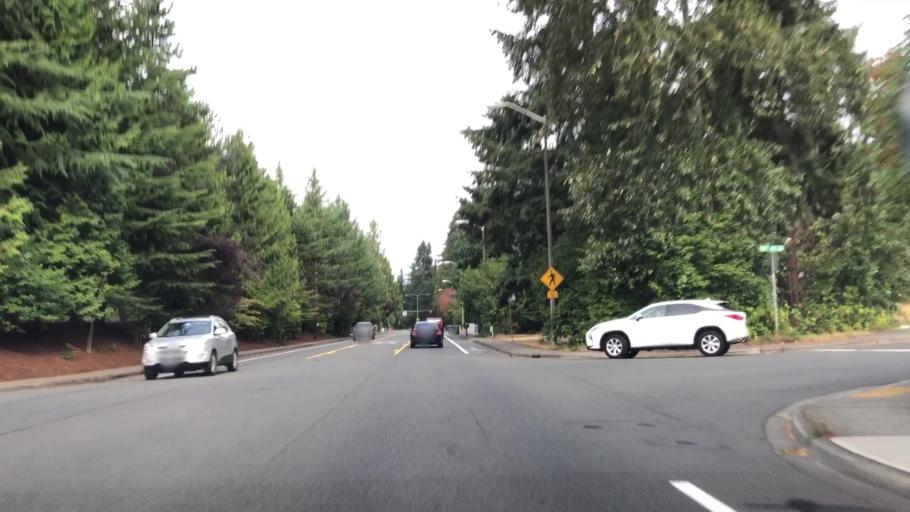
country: US
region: Washington
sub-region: King County
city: Kirkland
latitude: 47.6674
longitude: -122.1666
